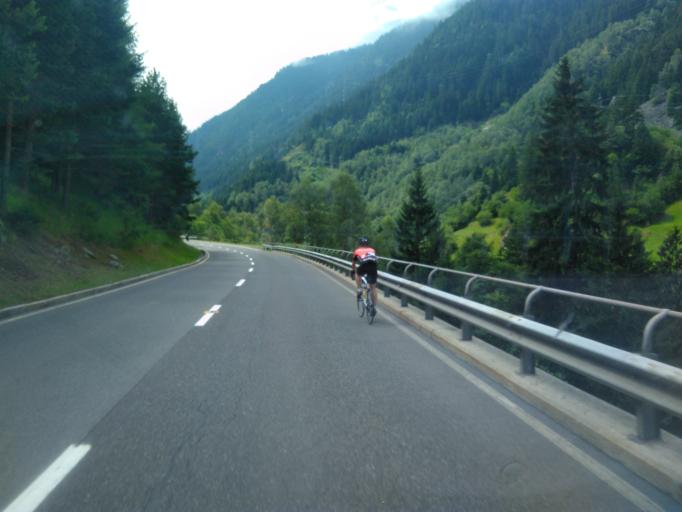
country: CH
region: Uri
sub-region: Uri
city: Andermatt
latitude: 46.6907
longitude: 8.5948
